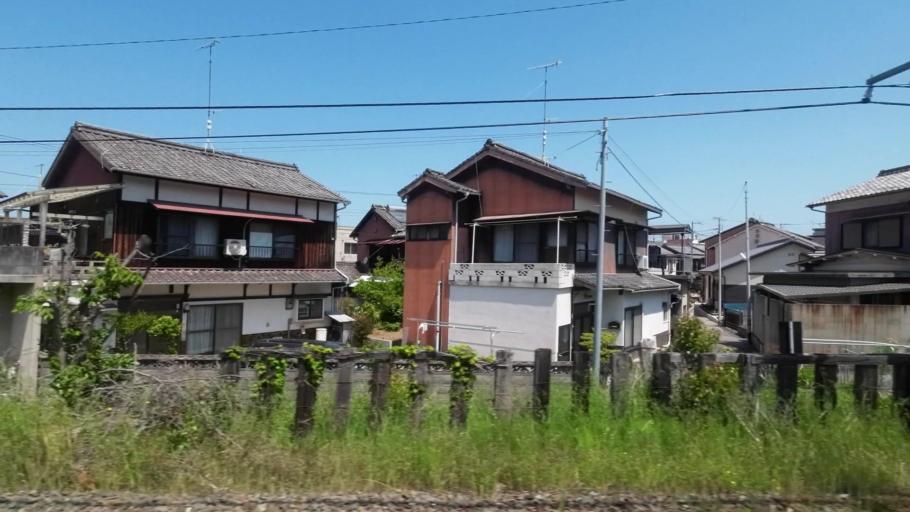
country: JP
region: Ehime
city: Hojo
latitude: 34.0332
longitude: 132.8400
